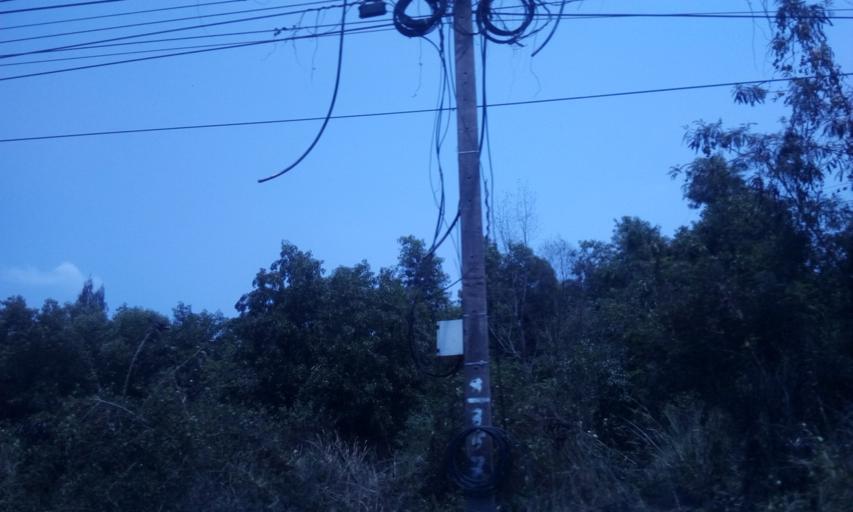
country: TH
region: Chachoengsao
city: Bang Nam Priao
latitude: 13.7706
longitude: 101.0671
